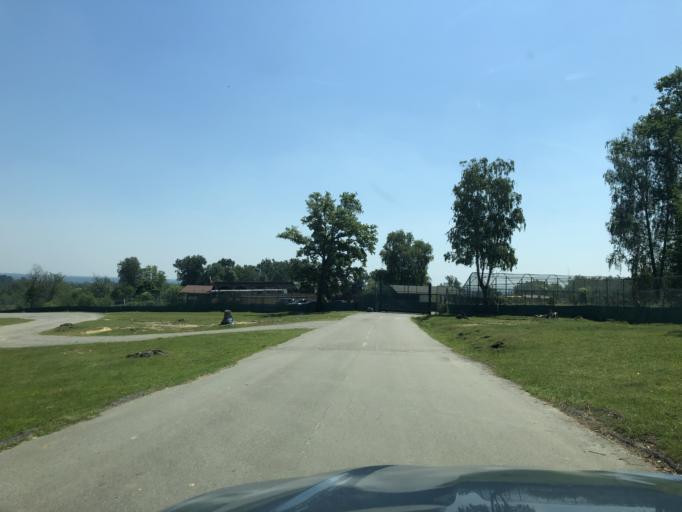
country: IT
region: Piedmont
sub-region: Provincia di Novara
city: Mezzomerico
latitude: 45.6394
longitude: 8.6116
